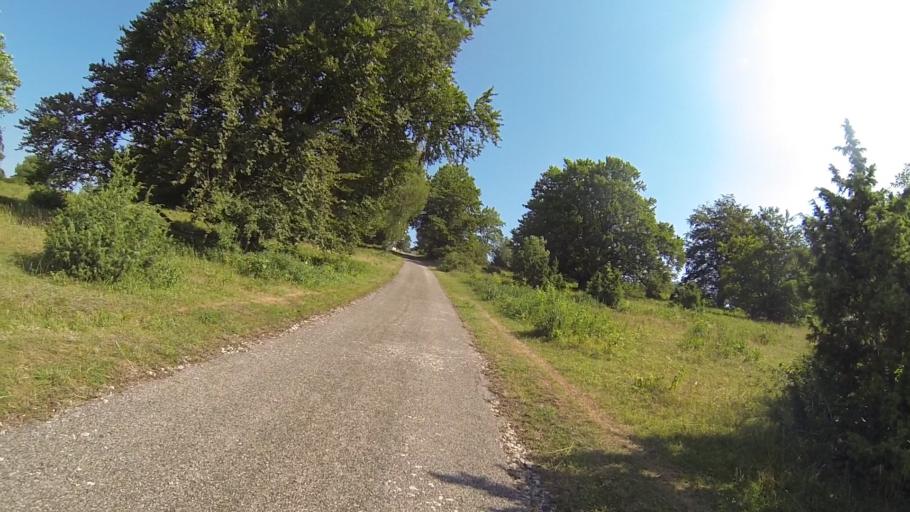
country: DE
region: Baden-Wuerttemberg
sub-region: Regierungsbezirk Stuttgart
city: Oberkochen
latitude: 48.7907
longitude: 10.0857
